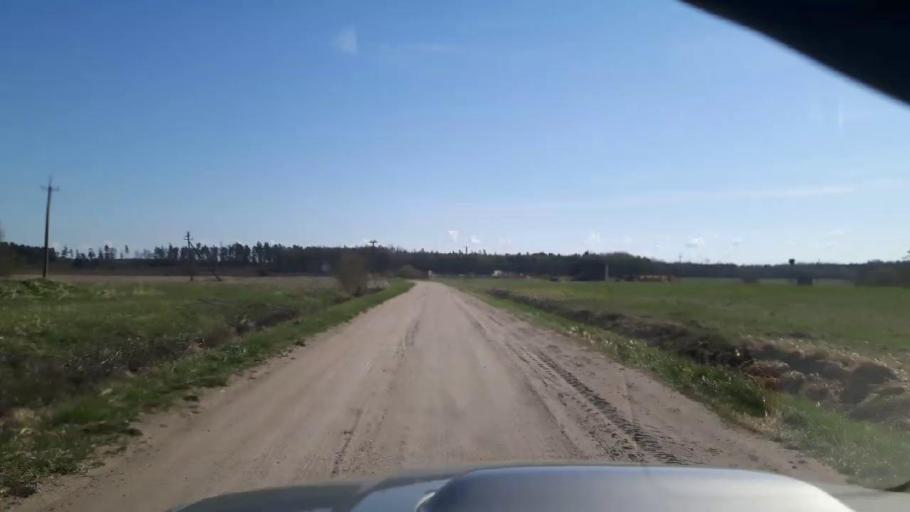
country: EE
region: Paernumaa
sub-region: Vaendra vald (alev)
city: Vandra
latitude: 58.5077
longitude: 24.9515
